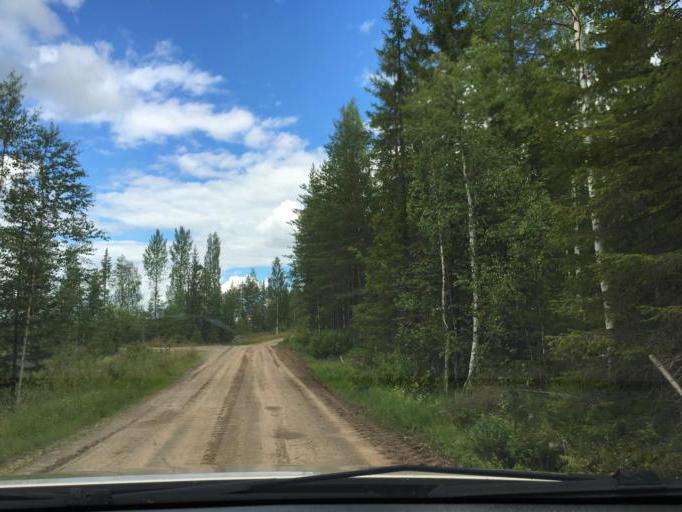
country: SE
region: Norrbotten
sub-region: Overkalix Kommun
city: OEverkalix
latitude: 66.1436
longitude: 22.7876
